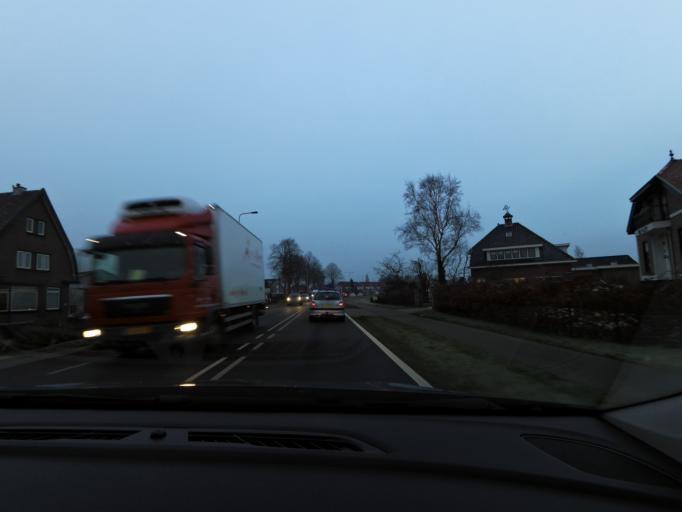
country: NL
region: Utrecht
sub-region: Gemeente Montfoort
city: Montfoort
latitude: 52.0398
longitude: 4.9401
